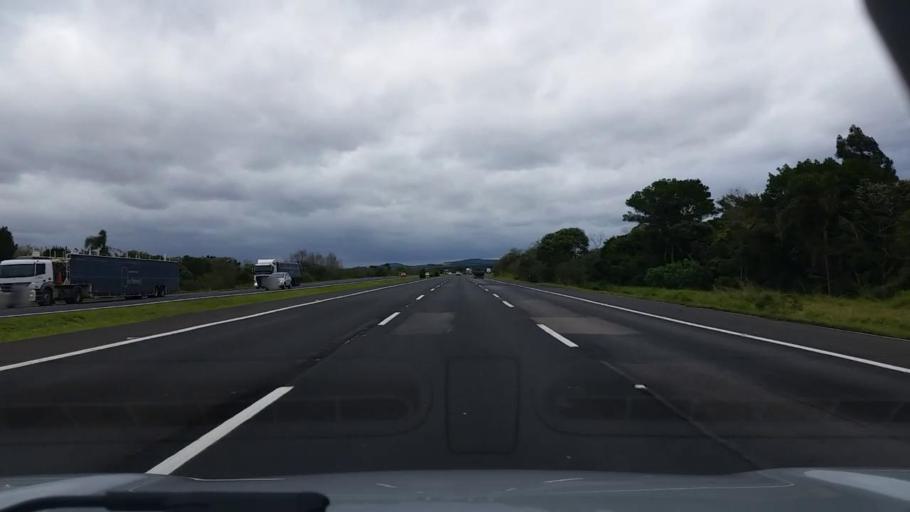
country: BR
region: Rio Grande do Sul
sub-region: Osorio
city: Osorio
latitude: -29.8783
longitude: -50.4299
